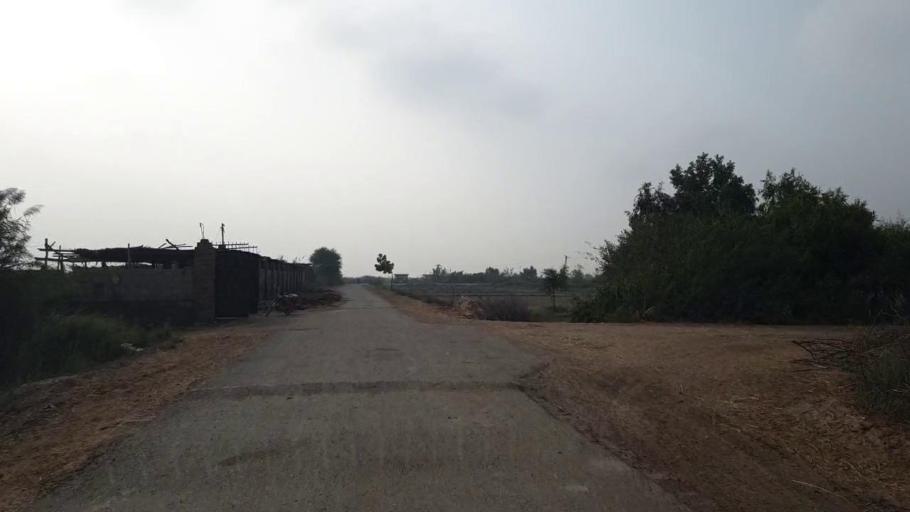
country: PK
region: Sindh
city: Tando Muhammad Khan
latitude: 25.1318
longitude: 68.5953
